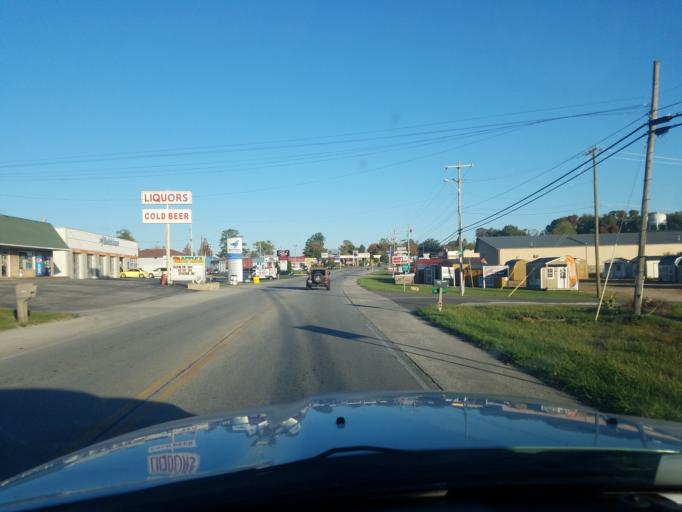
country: US
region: Indiana
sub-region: Washington County
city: Salem
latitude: 38.5976
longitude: -86.0840
